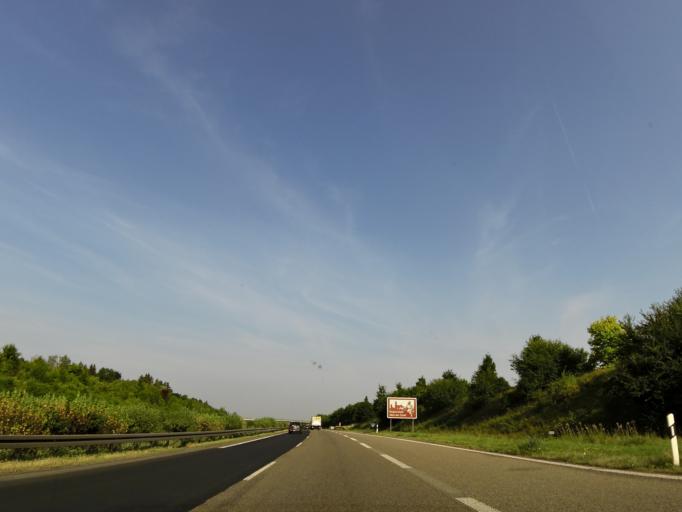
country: DE
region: Baden-Wuerttemberg
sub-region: Regierungsbezirk Stuttgart
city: Leonberg
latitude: 48.7823
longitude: 9.0102
